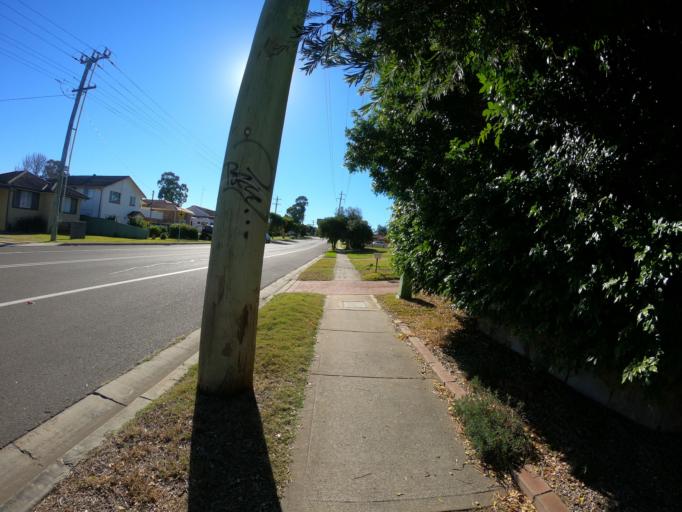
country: AU
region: New South Wales
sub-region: Hawkesbury
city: South Windsor
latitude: -33.6288
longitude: 150.7984
